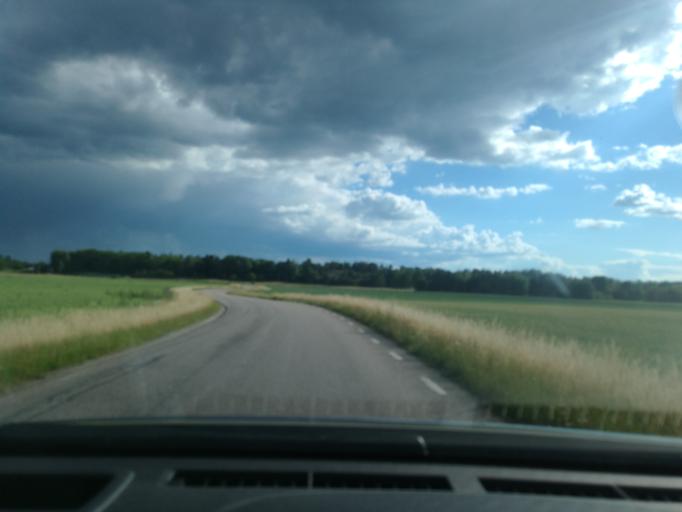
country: SE
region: Soedermanland
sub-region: Eskilstuna Kommun
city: Arla
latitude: 59.4182
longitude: 16.7060
